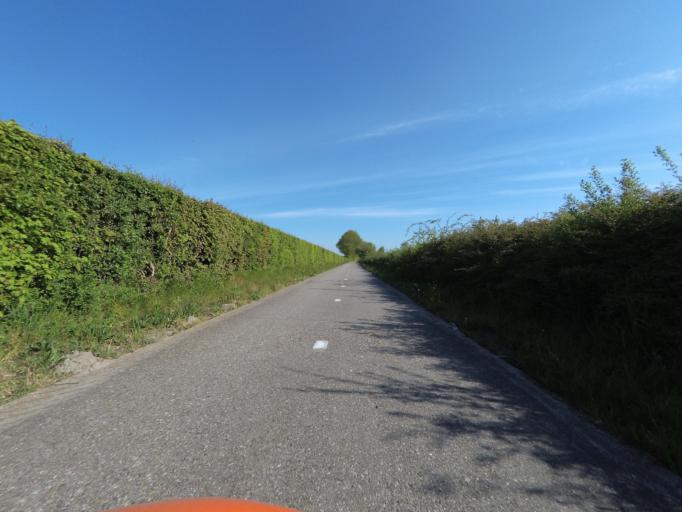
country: NL
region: Gelderland
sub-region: Gemeente Elburg
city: Elburg
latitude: 52.5100
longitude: 5.8525
